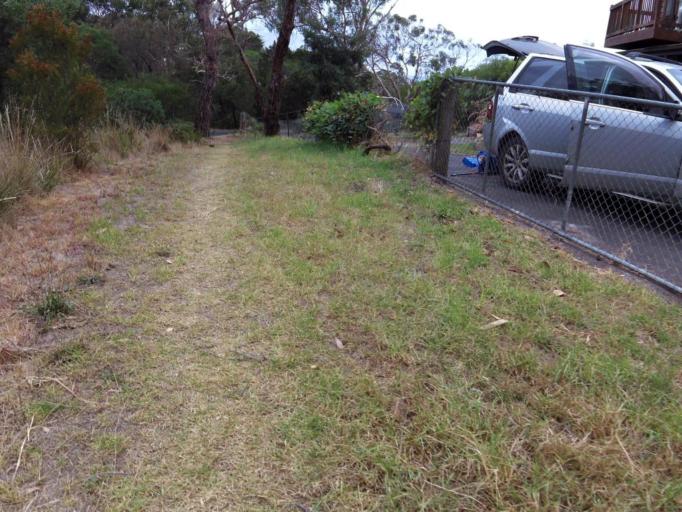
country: AU
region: Victoria
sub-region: Mornington Peninsula
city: Mount Martha
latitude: -38.2859
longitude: 145.0077
